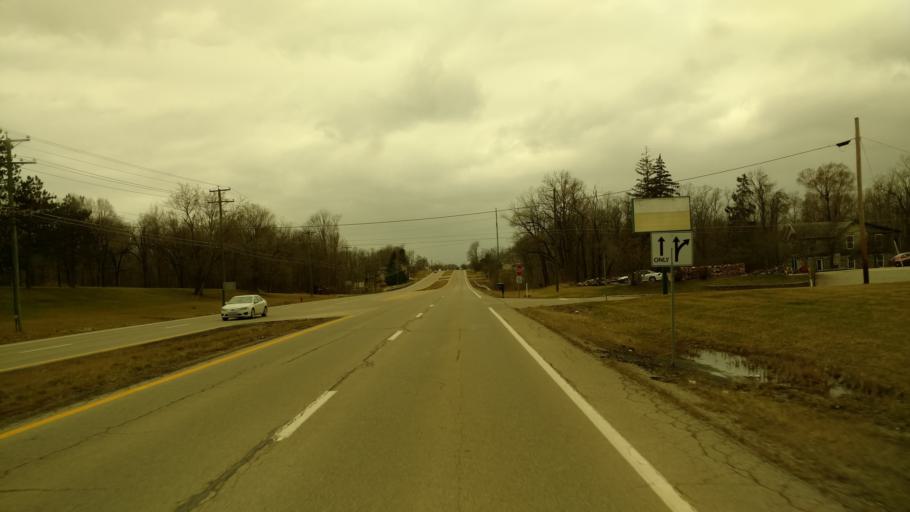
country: US
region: Ohio
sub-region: Licking County
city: Etna
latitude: 39.9580
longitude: -82.6505
